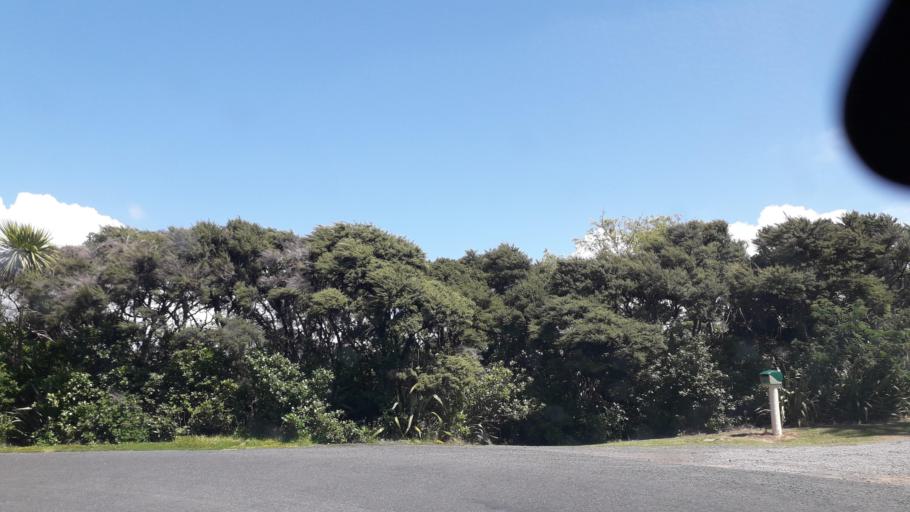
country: NZ
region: Northland
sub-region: Far North District
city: Paihia
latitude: -35.2224
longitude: 174.2588
